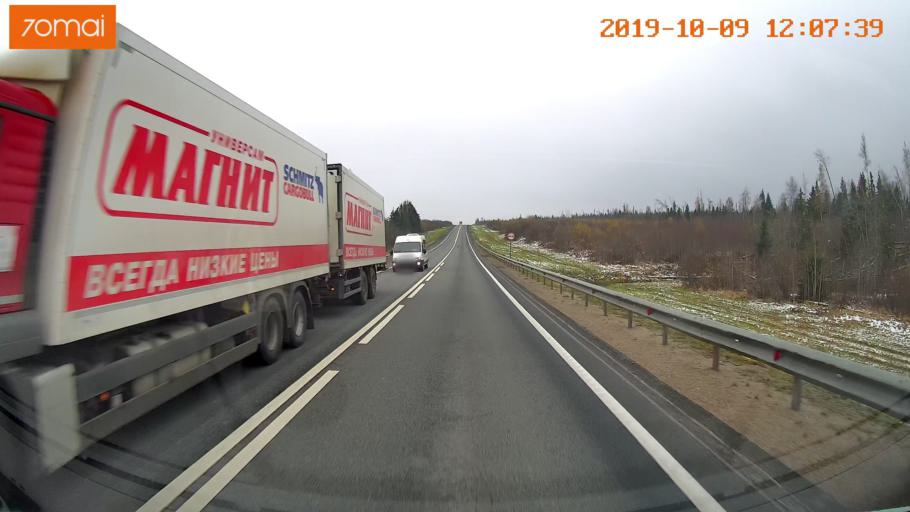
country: RU
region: Jaroslavl
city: Prechistoye
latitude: 58.5965
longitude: 40.3432
